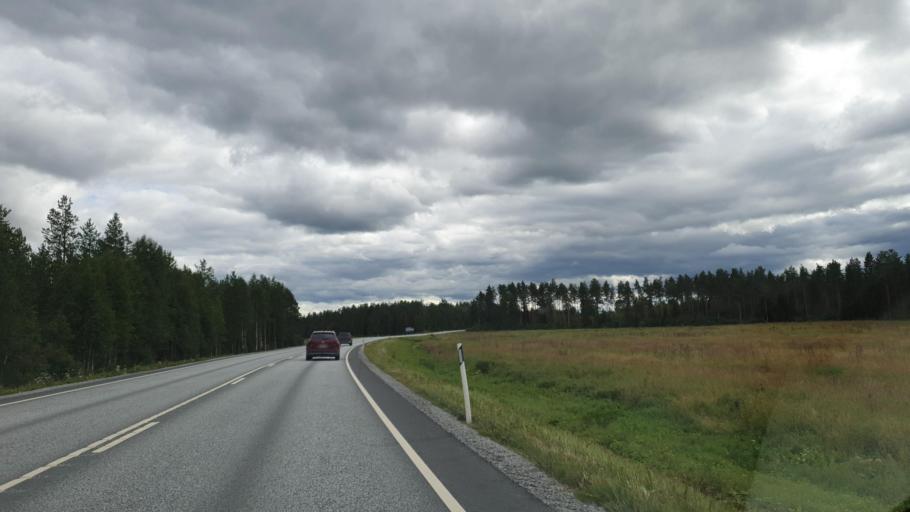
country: FI
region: Northern Savo
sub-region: Ylae-Savo
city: Sonkajaervi
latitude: 63.8858
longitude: 27.4374
